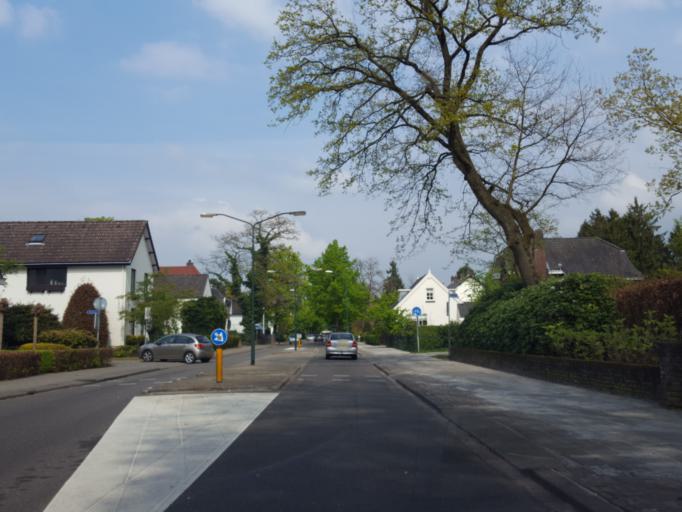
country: NL
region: North Brabant
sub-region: Gemeente Waalre
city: Waalre
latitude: 51.3892
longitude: 5.4527
